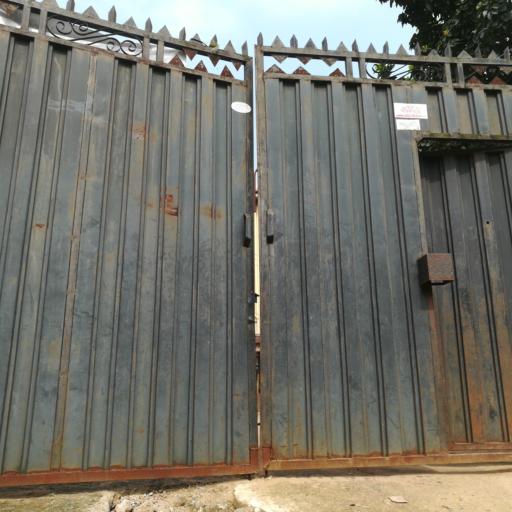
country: NG
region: Rivers
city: Port Harcourt
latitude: 4.8398
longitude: 7.0640
